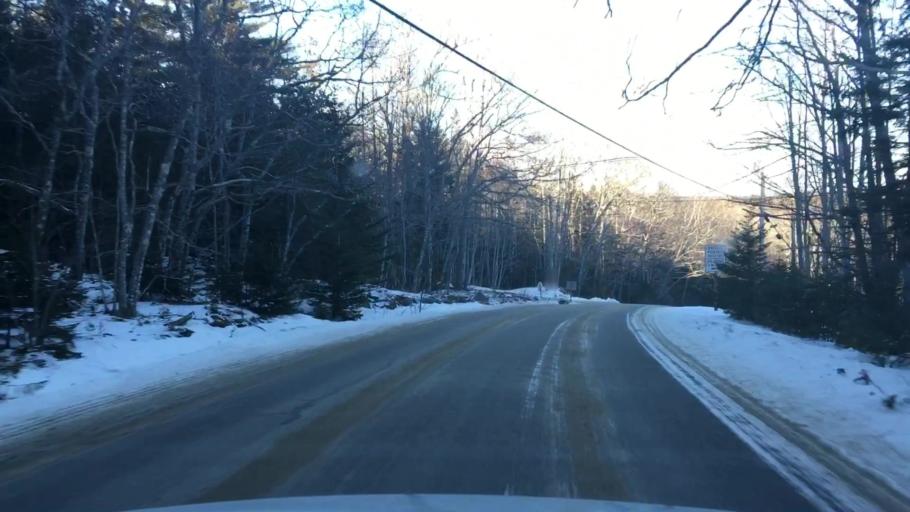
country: US
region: Maine
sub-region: Hancock County
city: Castine
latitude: 44.3557
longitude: -68.7784
